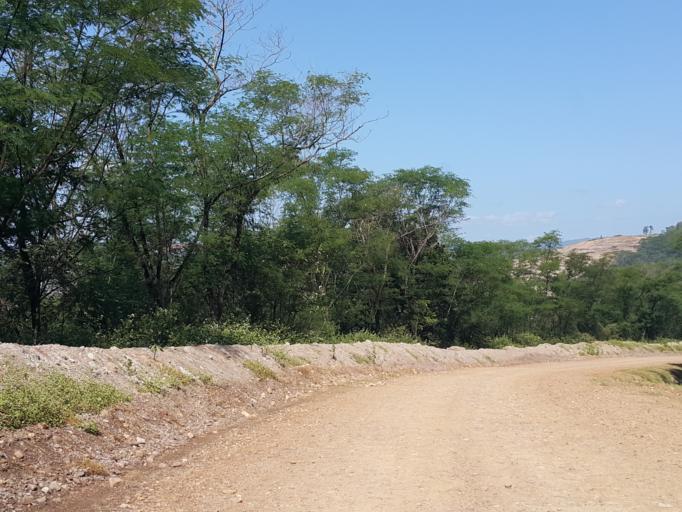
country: TH
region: Lampang
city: Mae Mo
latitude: 18.3255
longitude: 99.7394
